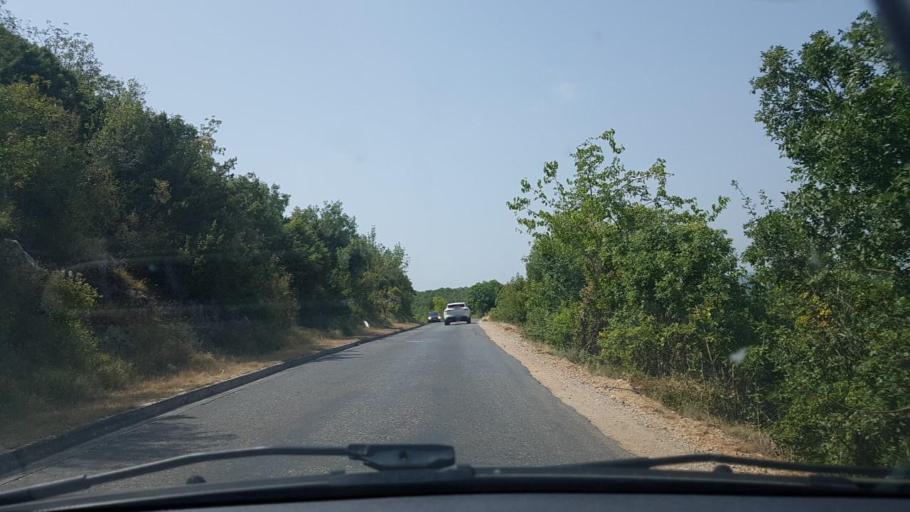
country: HR
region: Dubrovacko-Neretvanska
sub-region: Grad Dubrovnik
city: Metkovic
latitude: 43.0366
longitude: 17.7217
